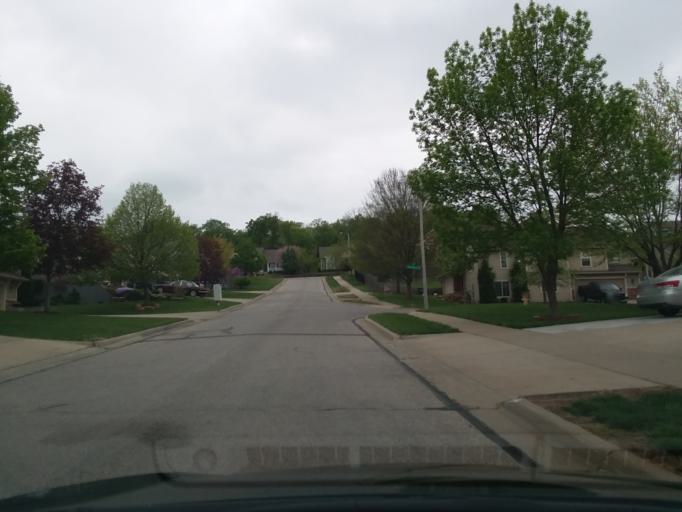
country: US
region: Kansas
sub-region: Douglas County
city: Lawrence
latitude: 38.9949
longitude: -95.2861
